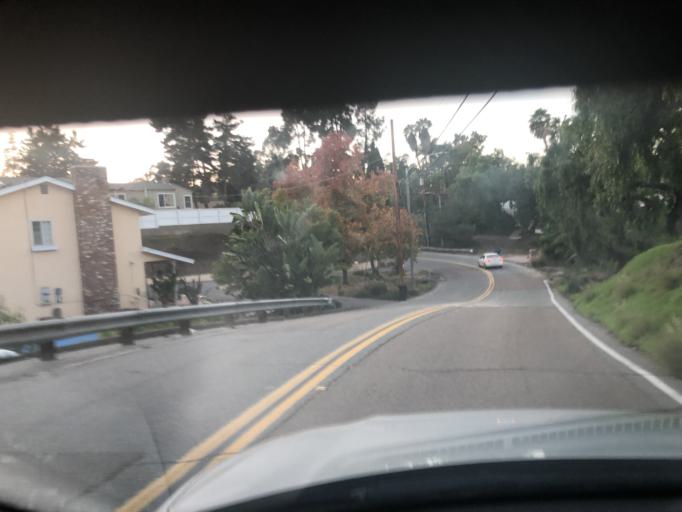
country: US
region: California
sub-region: San Diego County
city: Chula Vista
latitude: 32.6421
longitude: -117.0633
